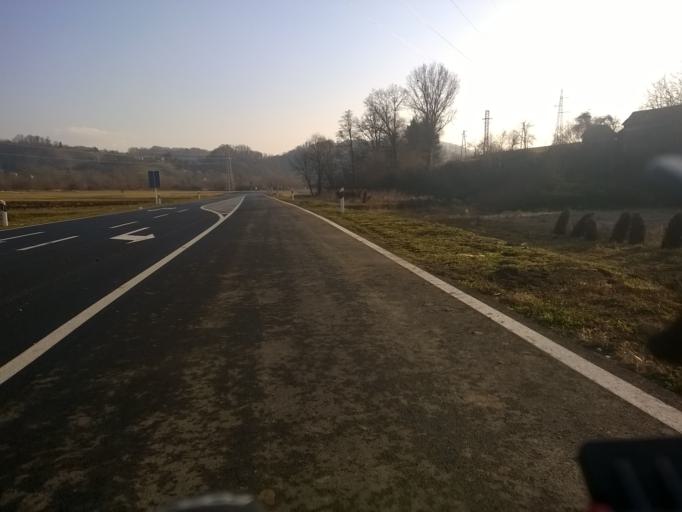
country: HR
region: Krapinsko-Zagorska
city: Zabok
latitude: 46.0371
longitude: 15.9194
